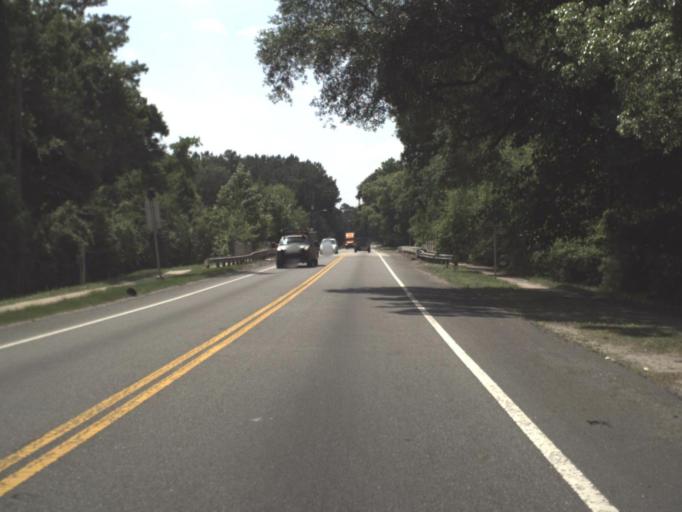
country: US
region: Florida
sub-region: Duval County
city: Jacksonville
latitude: 30.3716
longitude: -81.7469
